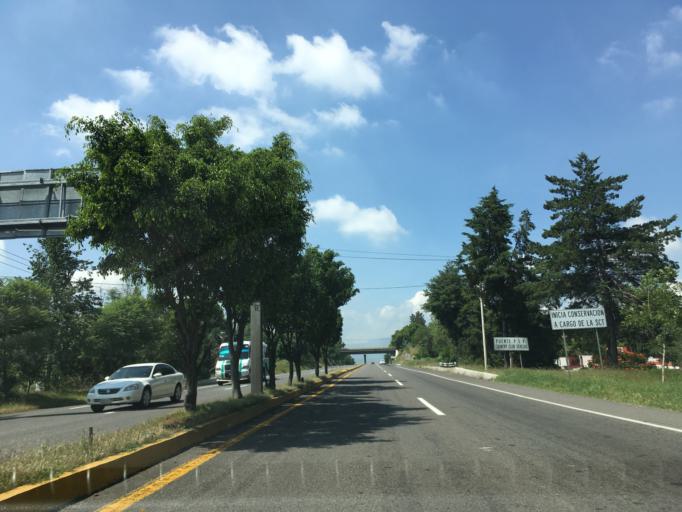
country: MX
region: Michoacan
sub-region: Morelia
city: Morelos
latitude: 19.6640
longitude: -101.2285
